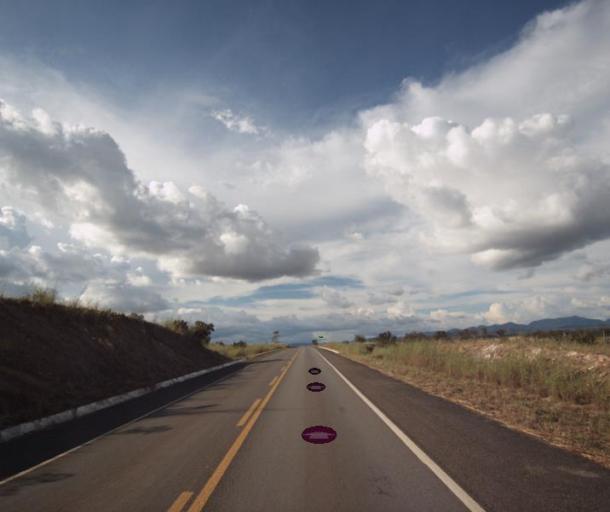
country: BR
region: Goias
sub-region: Barro Alto
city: Barro Alto
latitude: -14.8079
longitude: -48.6352
